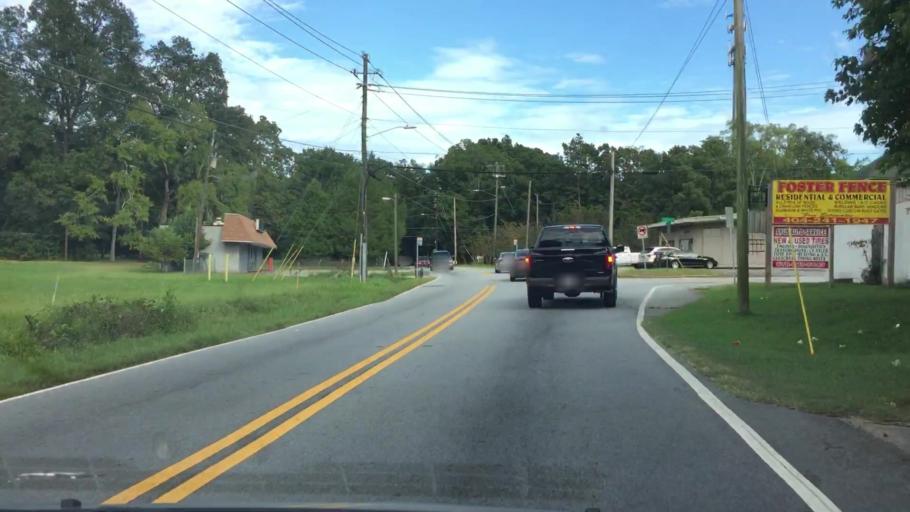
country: US
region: Georgia
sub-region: Clayton County
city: Conley
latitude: 33.6610
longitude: -84.3037
